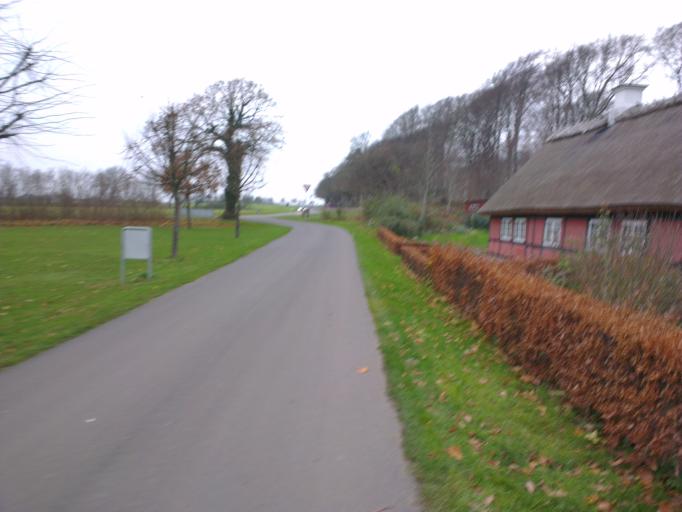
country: DK
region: Capital Region
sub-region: Frederikssund Kommune
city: Jaegerspris
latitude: 55.8580
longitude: 11.9733
